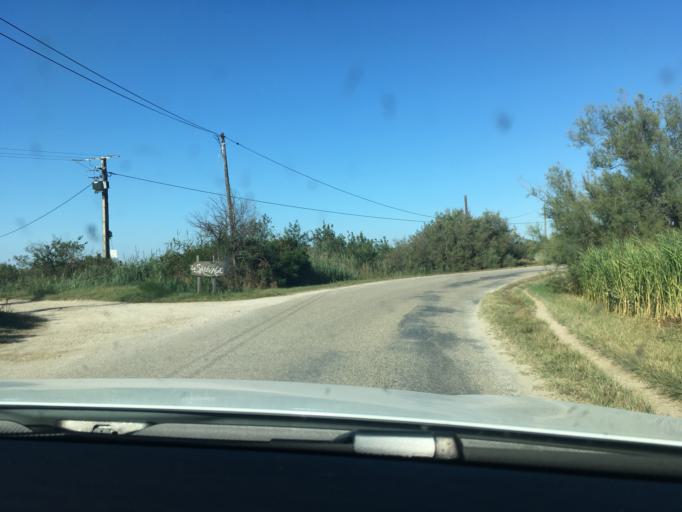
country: FR
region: Provence-Alpes-Cote d'Azur
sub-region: Departement des Bouches-du-Rhone
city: Saintes-Maries-de-la-Mer
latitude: 43.4871
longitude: 4.3799
